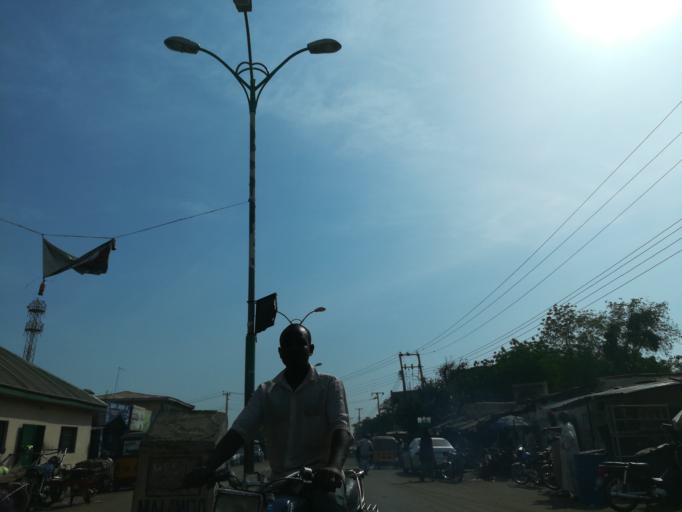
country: NG
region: Kano
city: Kano
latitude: 12.0159
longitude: 8.5233
